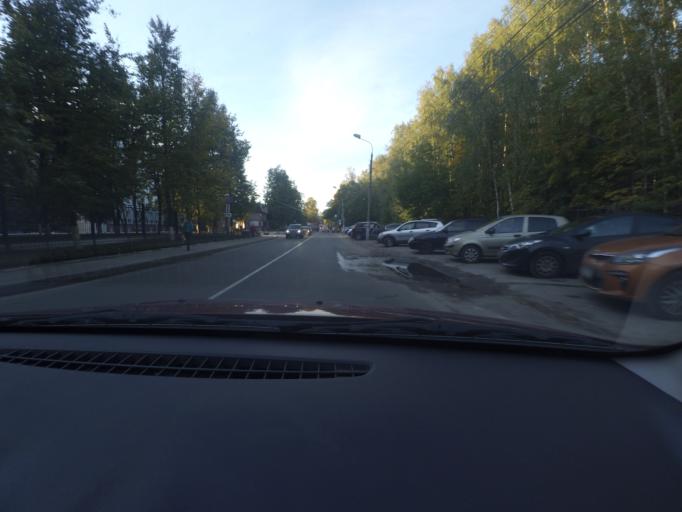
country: RU
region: Nizjnij Novgorod
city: Nizhniy Novgorod
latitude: 56.2707
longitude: 43.9936
